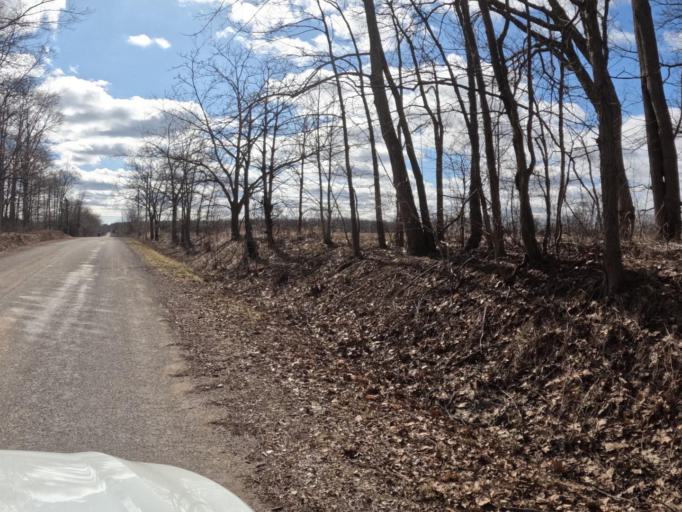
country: CA
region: Ontario
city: Norfolk County
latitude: 42.7542
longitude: -80.2788
